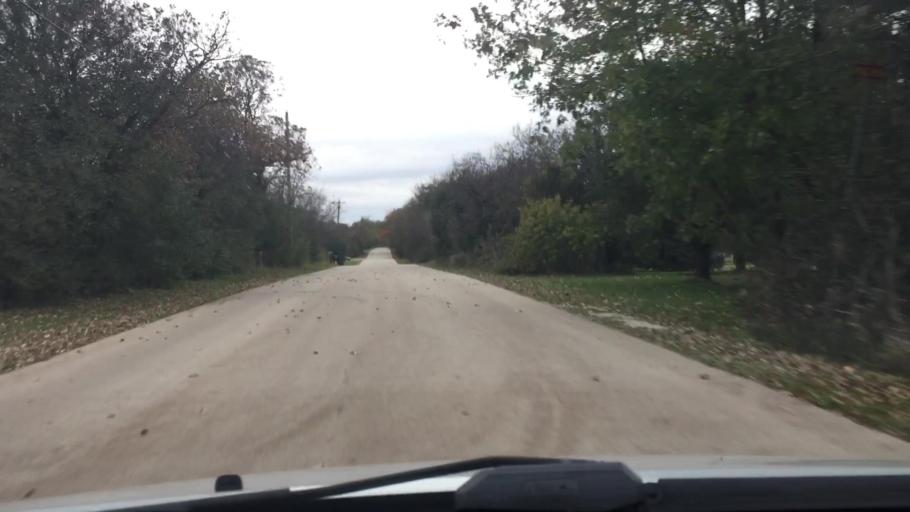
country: US
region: Wisconsin
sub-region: Waukesha County
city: North Prairie
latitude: 42.9303
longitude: -88.4330
